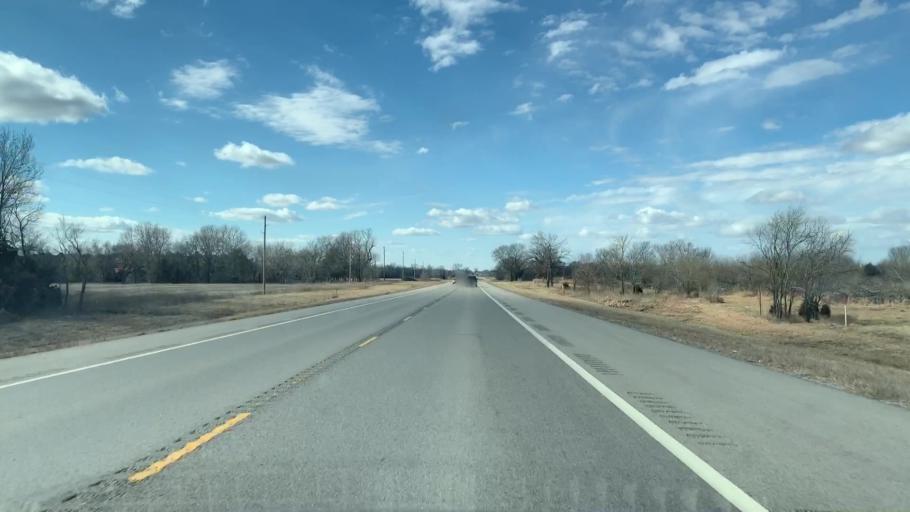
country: US
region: Kansas
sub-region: Labette County
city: Oswego
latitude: 37.3400
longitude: -95.0638
